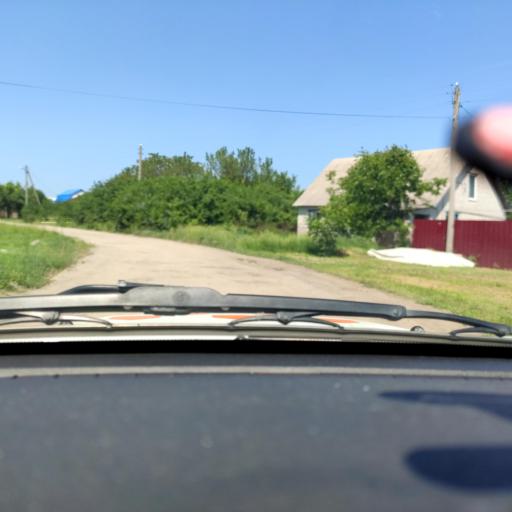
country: RU
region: Voronezj
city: Devitsa
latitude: 51.5956
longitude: 38.9905
